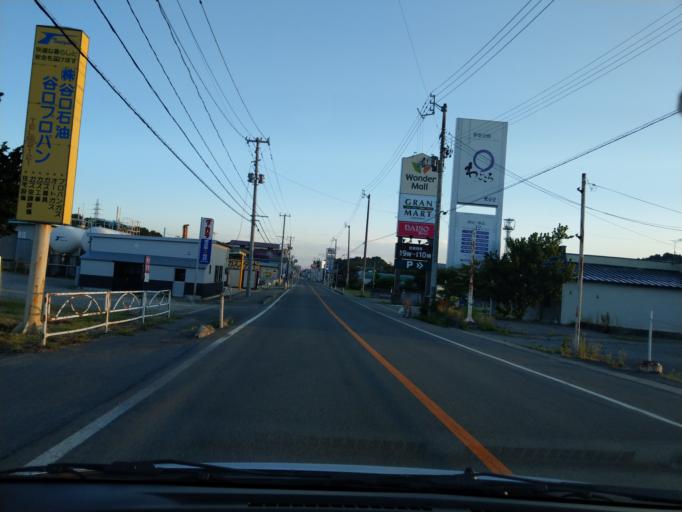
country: JP
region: Akita
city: Kakunodatemachi
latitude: 39.5932
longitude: 140.5760
